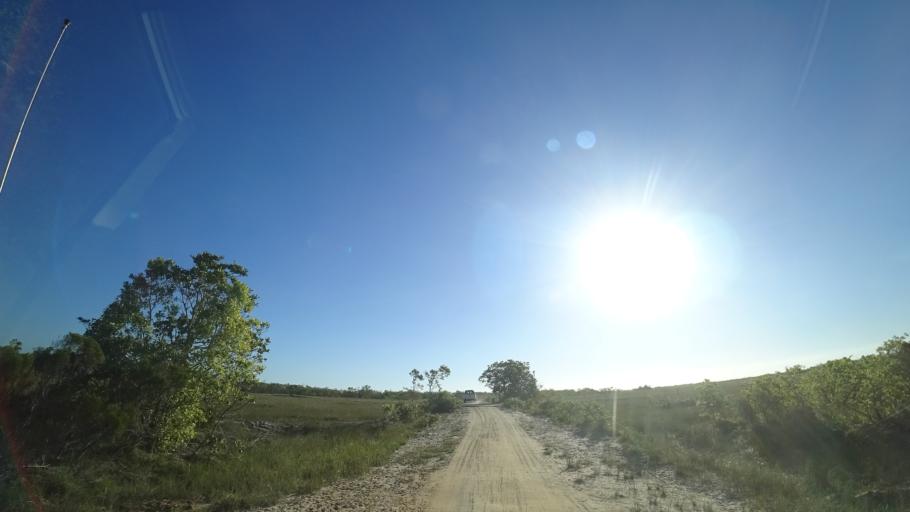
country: MZ
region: Sofala
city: Beira
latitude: -19.5760
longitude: 35.2034
